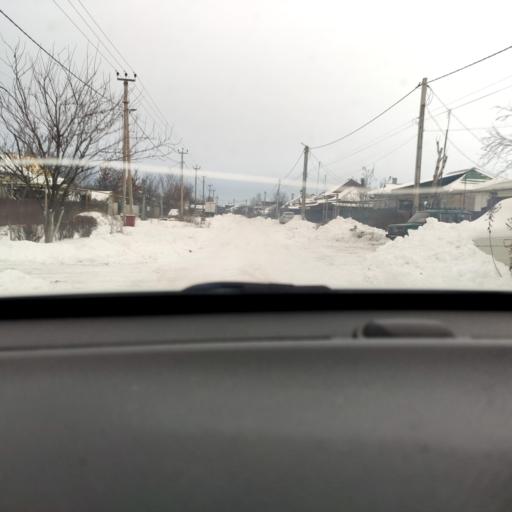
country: RU
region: Voronezj
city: Volya
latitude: 51.7526
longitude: 39.4997
